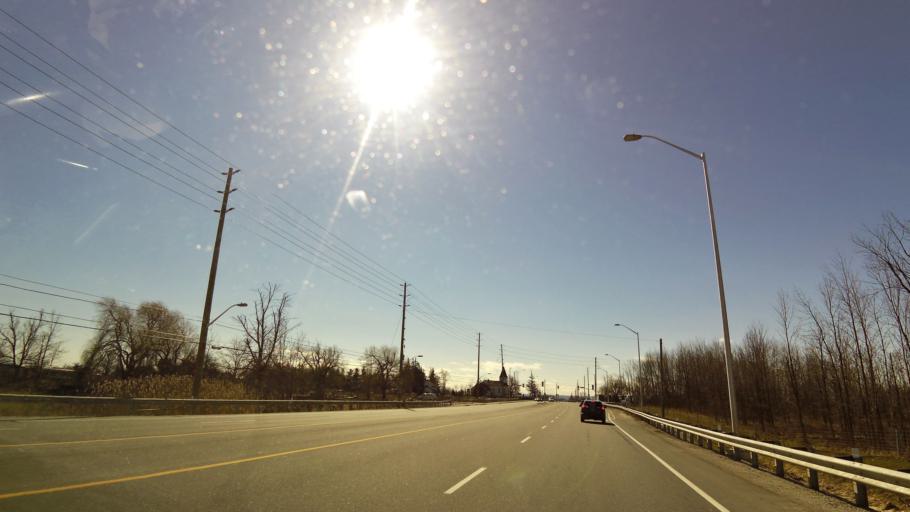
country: CA
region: Ontario
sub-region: Halton
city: Milton
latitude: 43.5896
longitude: -79.8181
